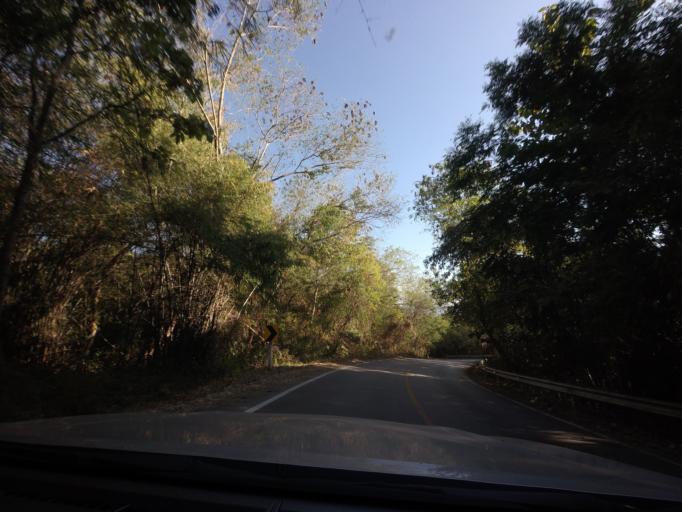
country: TH
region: Lampang
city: Chae Hom
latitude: 18.5468
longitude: 99.6363
